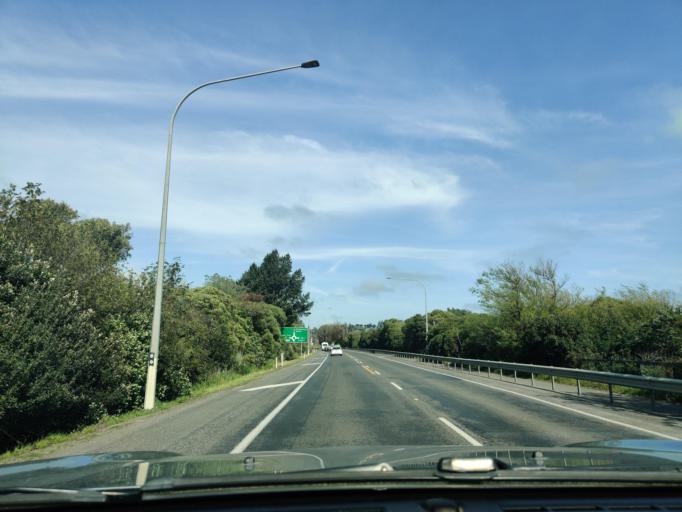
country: NZ
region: Manawatu-Wanganui
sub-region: Wanganui District
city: Wanganui
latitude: -39.9465
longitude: 175.0481
